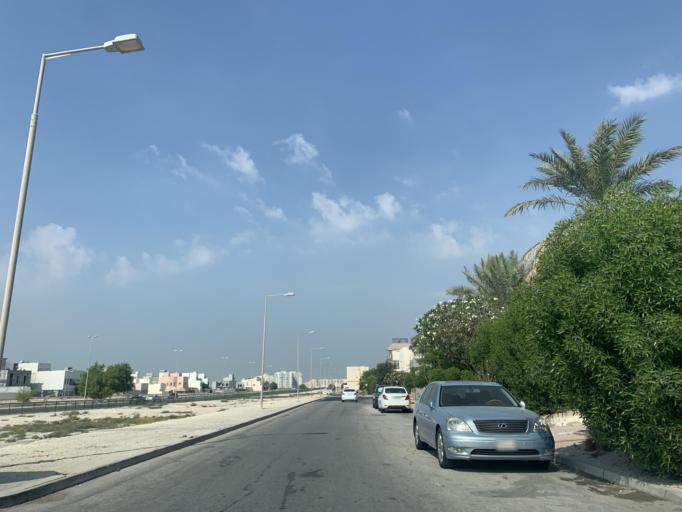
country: BH
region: Central Governorate
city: Madinat Hamad
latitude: 26.1064
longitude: 50.4980
